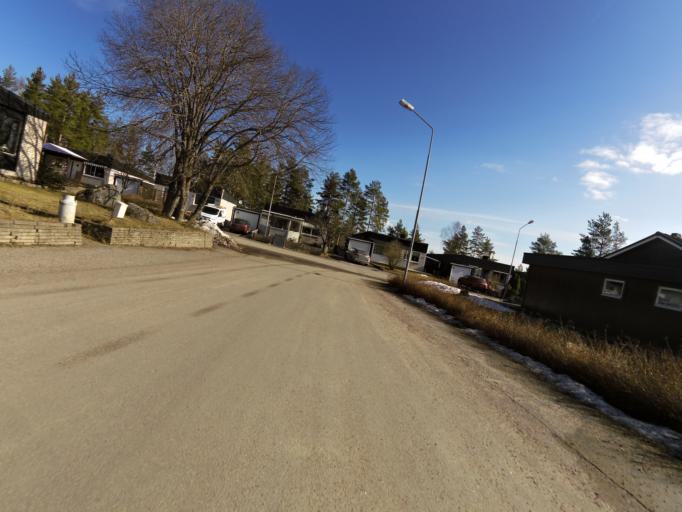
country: SE
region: Gaevleborg
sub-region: Hofors Kommun
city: Hofors
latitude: 60.5541
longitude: 16.2740
